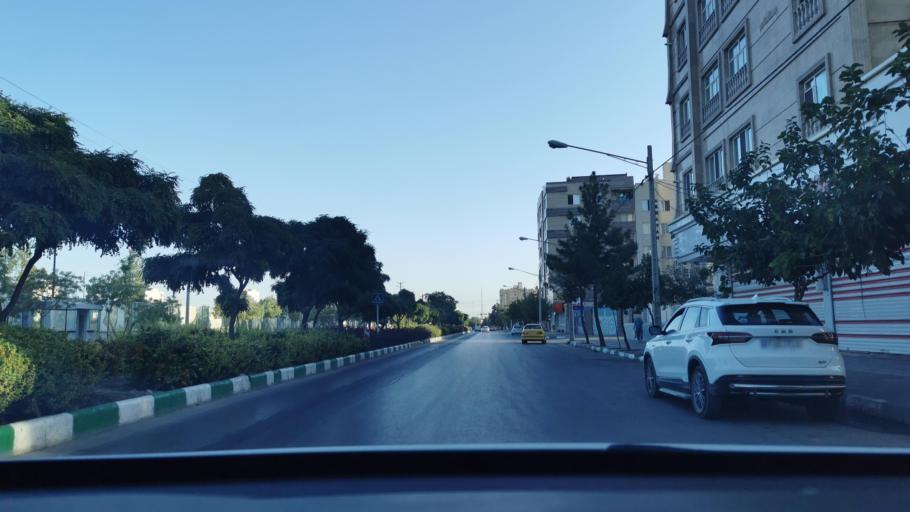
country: IR
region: Razavi Khorasan
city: Mashhad
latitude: 36.3496
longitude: 59.5139
